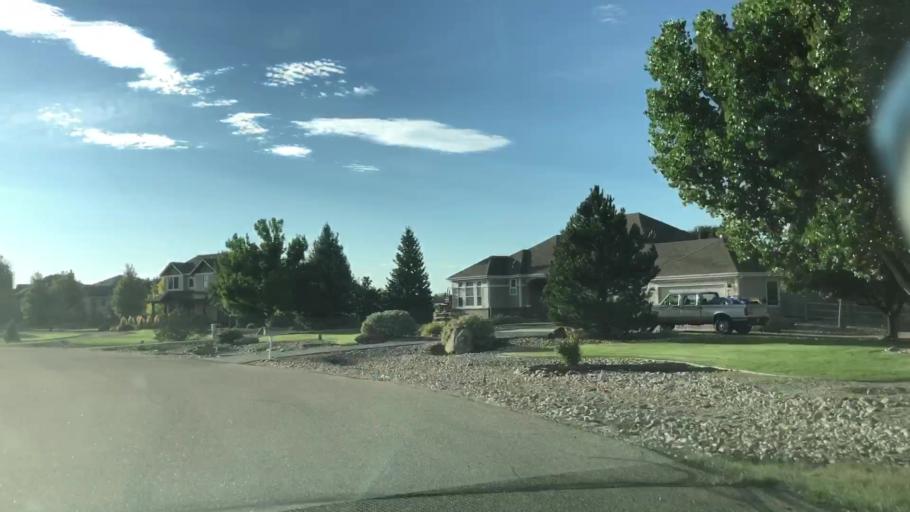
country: US
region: Colorado
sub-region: Weld County
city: Windsor
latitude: 40.4416
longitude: -104.9492
